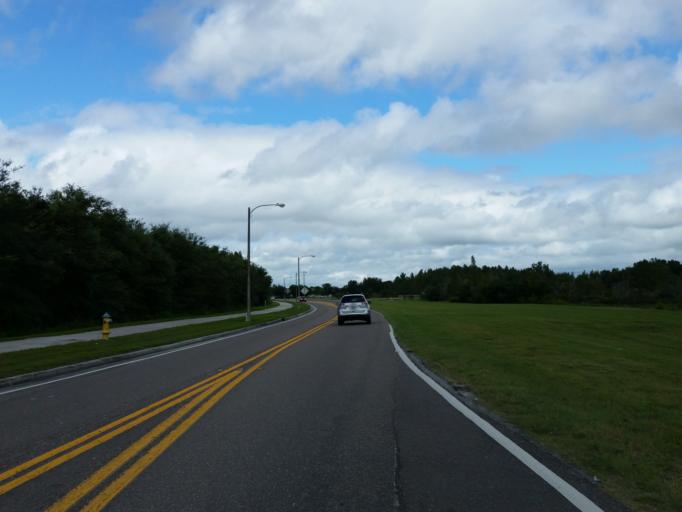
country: US
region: Florida
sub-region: Pasco County
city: Wesley Chapel
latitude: 28.2013
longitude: -82.2991
